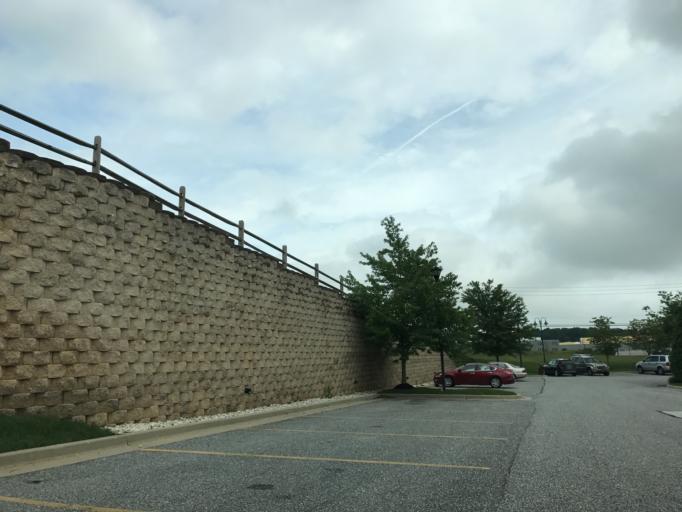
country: US
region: Pennsylvania
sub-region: York County
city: Shrewsbury
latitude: 39.7729
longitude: -76.6646
